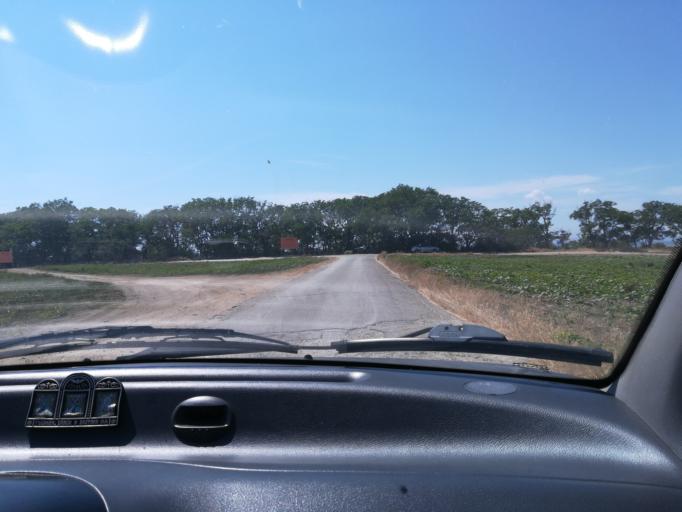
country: RU
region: Krasnodarskiy
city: Blagovetschenskaya
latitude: 45.0682
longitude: 37.0564
